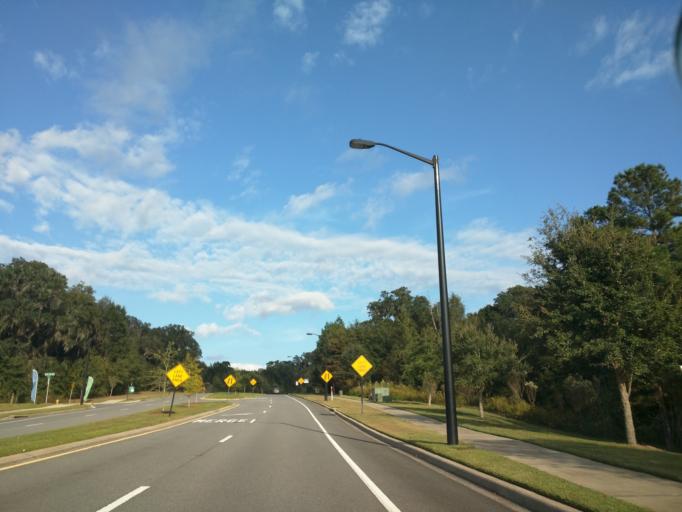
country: US
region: Florida
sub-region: Leon County
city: Tallahassee
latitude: 30.4116
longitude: -84.2317
